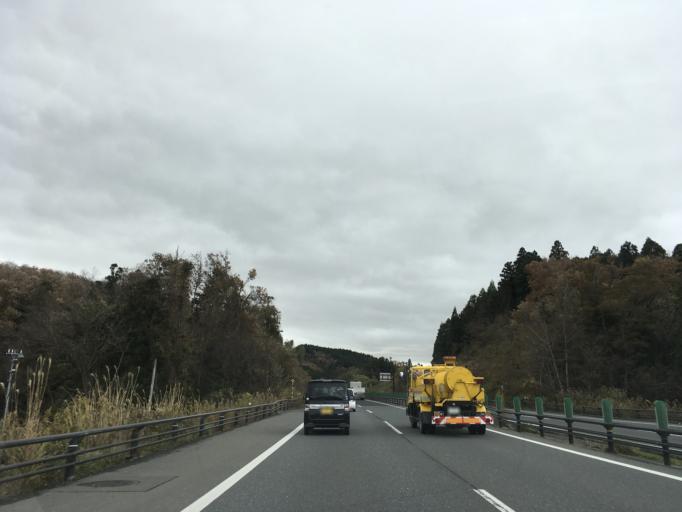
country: JP
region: Miyagi
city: Wakuya
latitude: 38.5542
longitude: 141.2703
